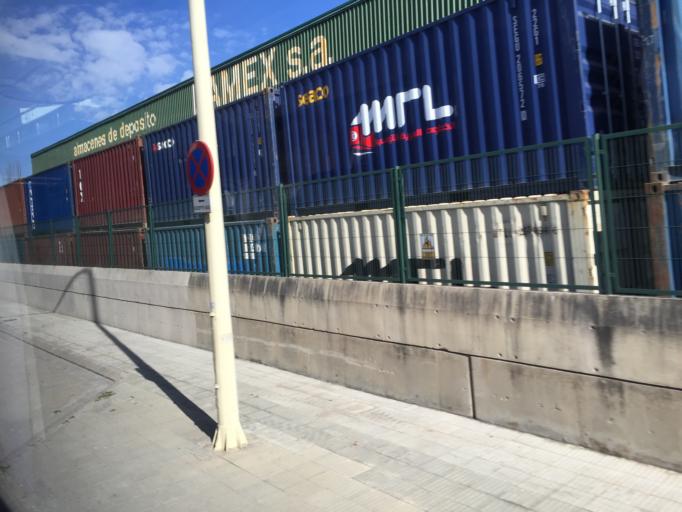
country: ES
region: Catalonia
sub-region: Provincia de Barcelona
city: Sants-Montjuic
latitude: 41.3421
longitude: 2.1447
